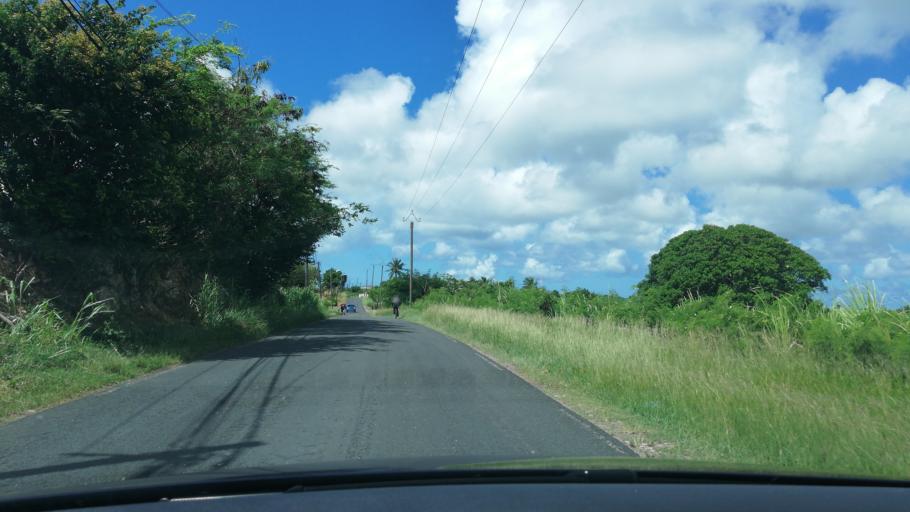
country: GP
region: Guadeloupe
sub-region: Guadeloupe
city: Petit-Canal
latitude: 16.3797
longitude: -61.4396
